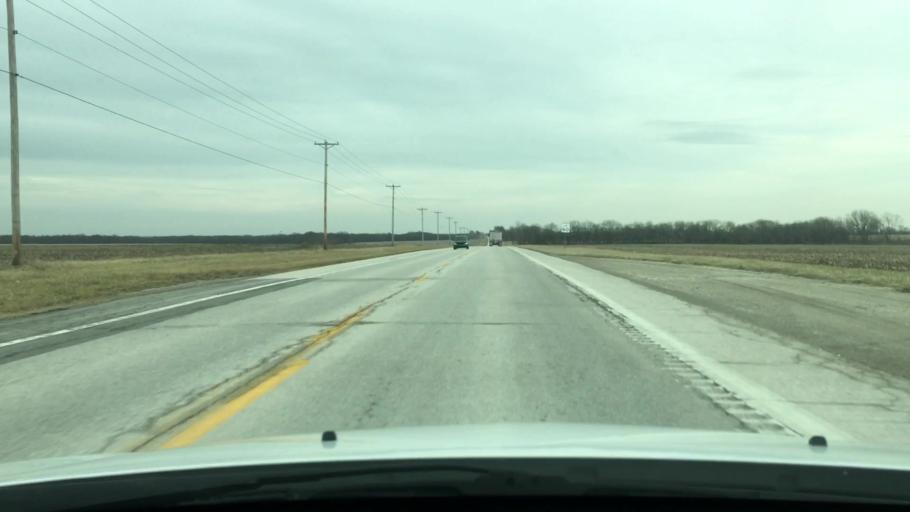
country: US
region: Missouri
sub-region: Pike County
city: Bowling Green
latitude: 39.3445
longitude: -91.2964
